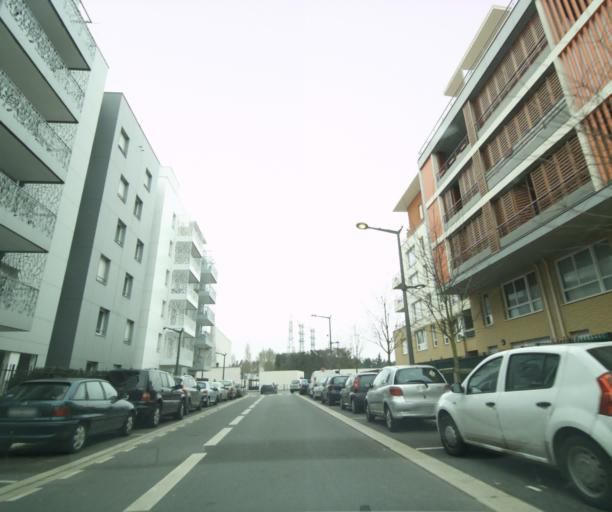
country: FR
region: Ile-de-France
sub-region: Departement du Val-d'Oise
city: Courdimanche
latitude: 49.0519
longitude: 2.0082
